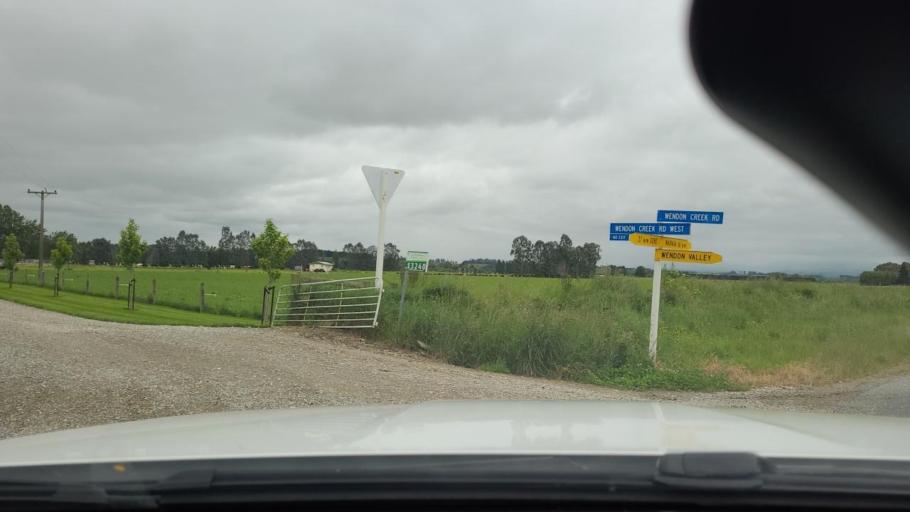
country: NZ
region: Southland
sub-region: Gore District
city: Gore
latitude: -45.8404
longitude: 168.7999
